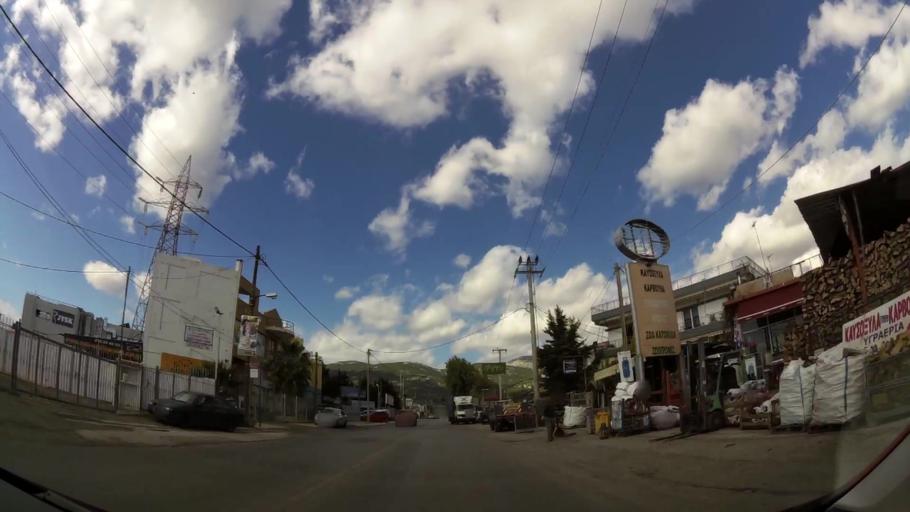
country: GR
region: Attica
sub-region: Nomarchia Anatolikis Attikis
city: Acharnes
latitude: 38.1012
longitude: 23.7428
